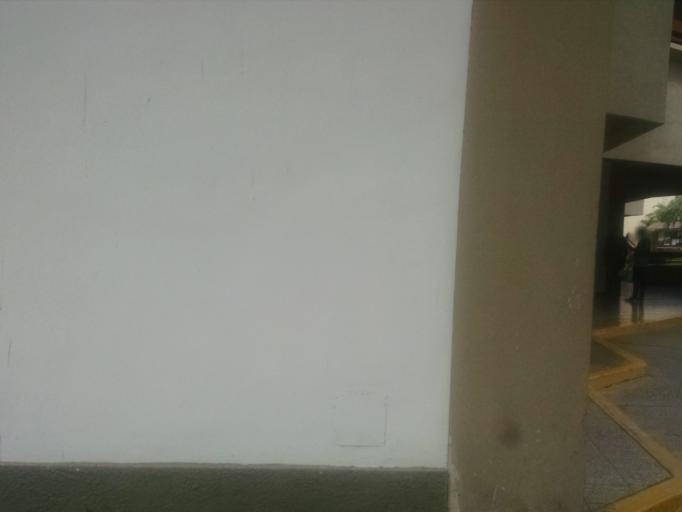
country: PE
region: Piura
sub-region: Provincia de Piura
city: Piura
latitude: -5.1776
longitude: -80.6350
